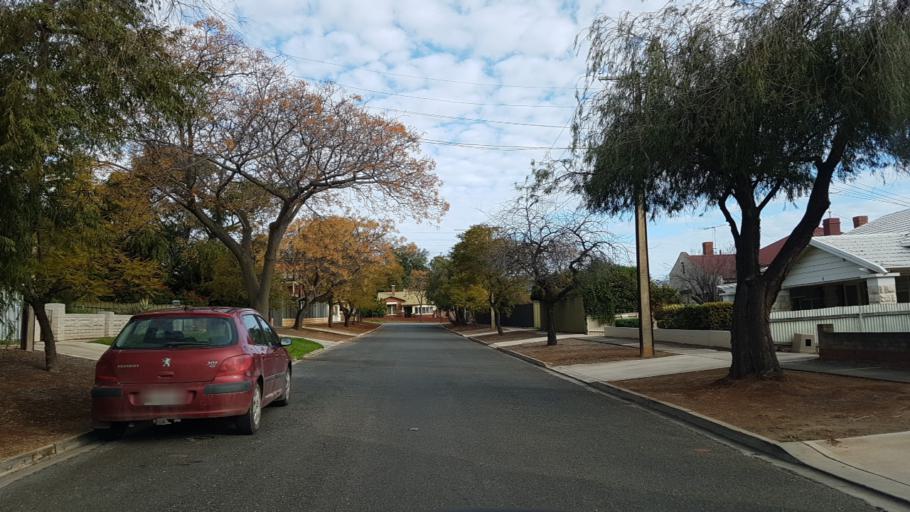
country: AU
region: South Australia
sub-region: Prospect
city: Prospect
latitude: -34.8763
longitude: 138.5906
